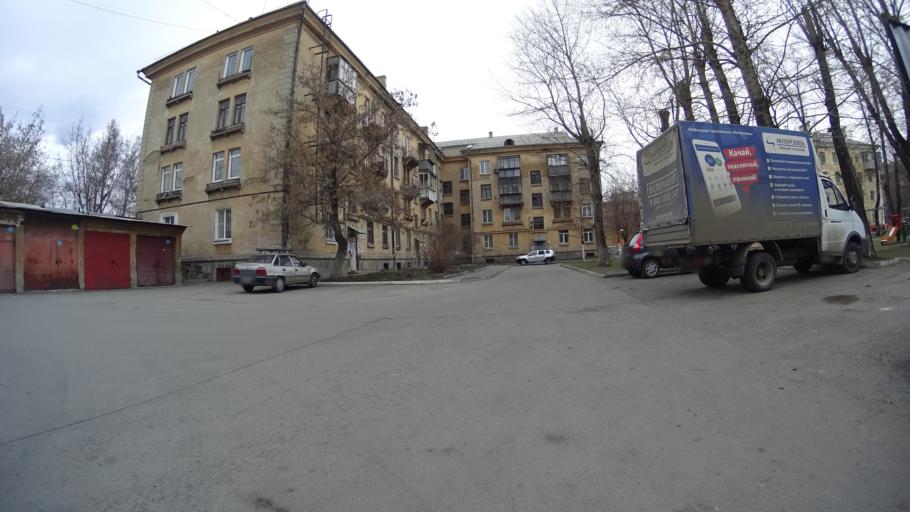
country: RU
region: Chelyabinsk
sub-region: Gorod Chelyabinsk
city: Chelyabinsk
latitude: 55.1641
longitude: 61.4392
